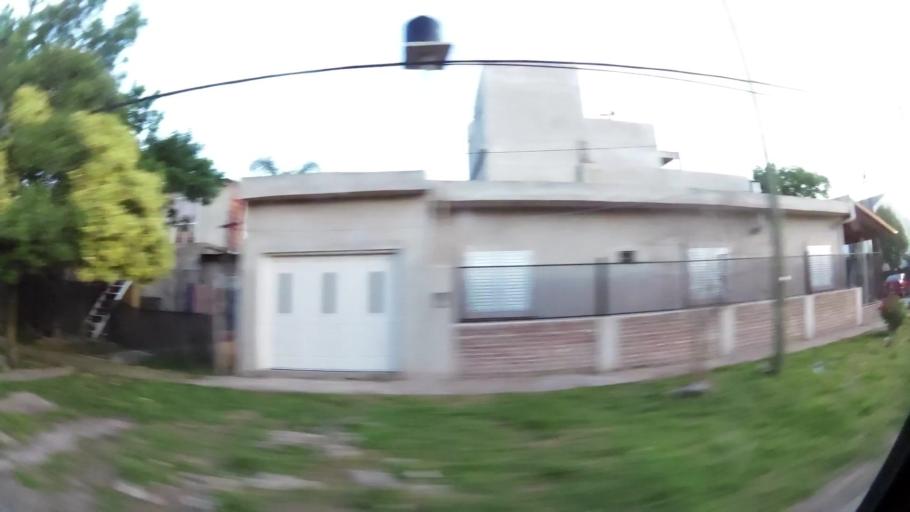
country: AR
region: Buenos Aires
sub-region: Partido de Quilmes
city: Quilmes
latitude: -34.7803
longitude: -58.2236
